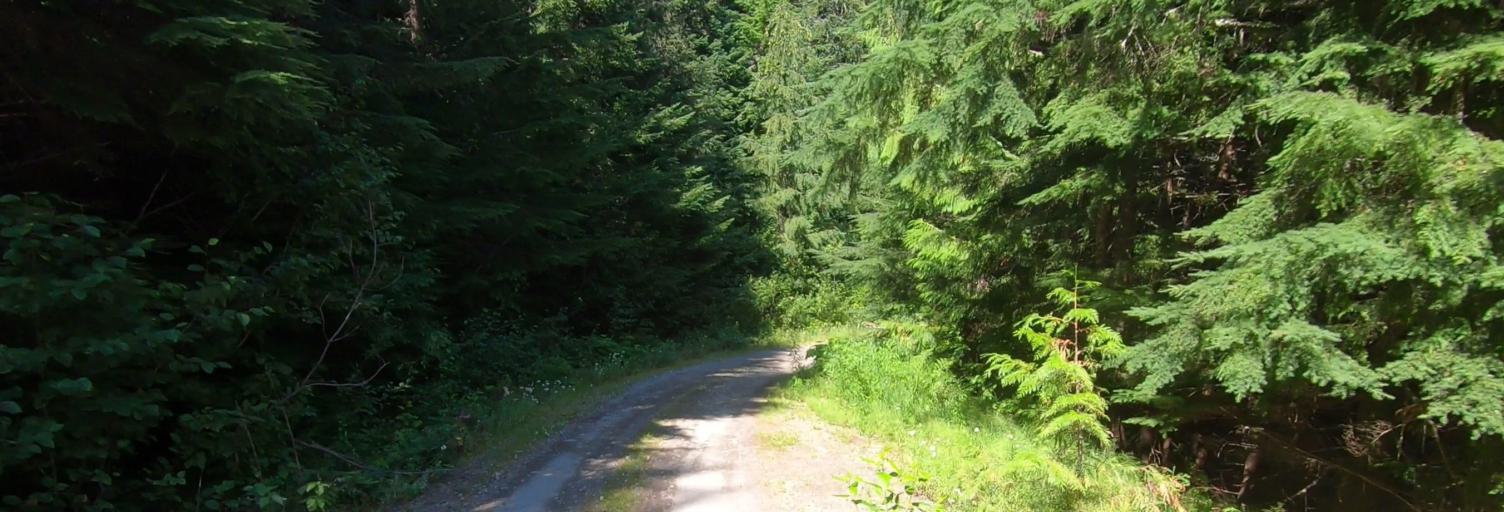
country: CA
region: British Columbia
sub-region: Fraser Valley Regional District
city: Chilliwack
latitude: 48.8629
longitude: -121.7832
